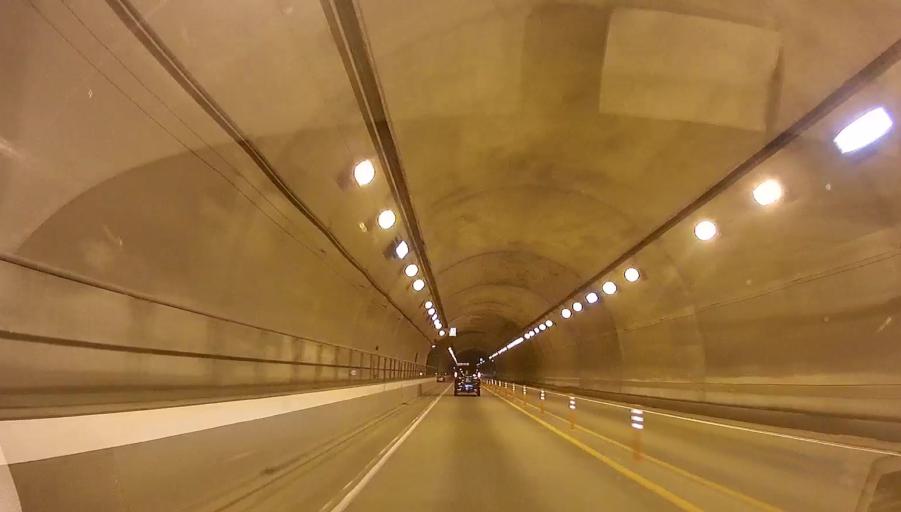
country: JP
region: Hokkaido
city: Shimo-furano
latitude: 43.0510
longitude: 142.4940
